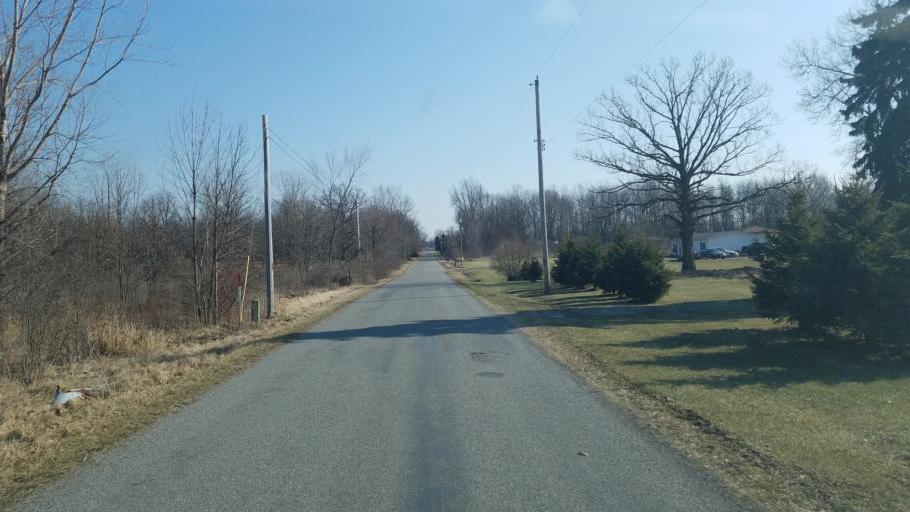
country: US
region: Ohio
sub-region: Crawford County
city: Crestline
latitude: 40.7798
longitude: -82.7585
